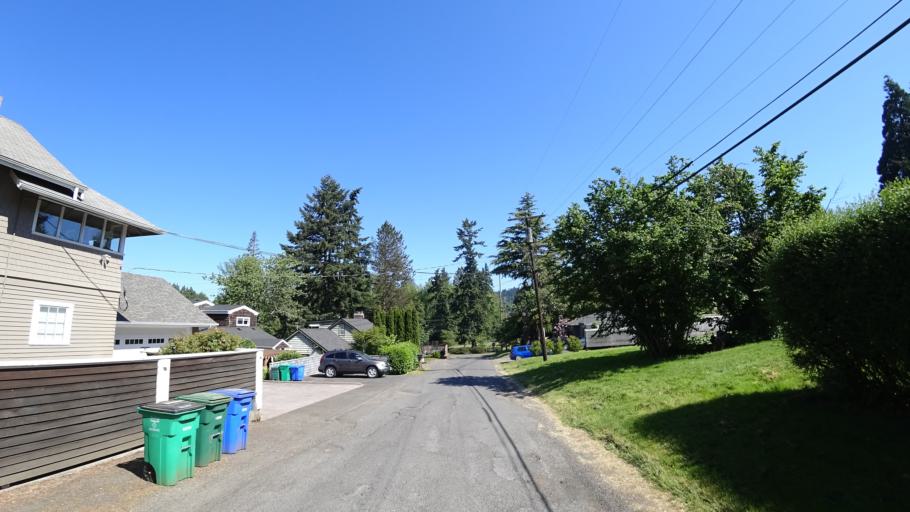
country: US
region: Oregon
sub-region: Washington County
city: Raleigh Hills
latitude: 45.4828
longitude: -122.7269
